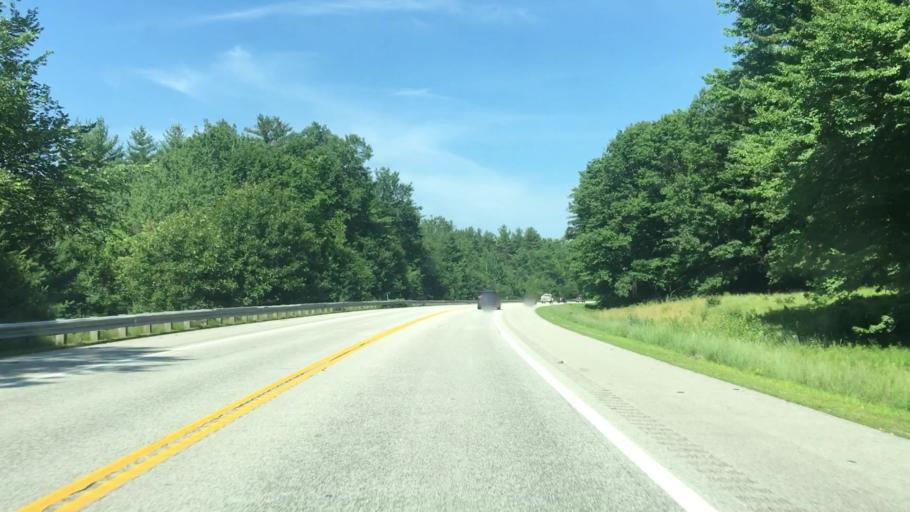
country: US
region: New Hampshire
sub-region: Merrimack County
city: Henniker
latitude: 43.1853
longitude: -71.7983
